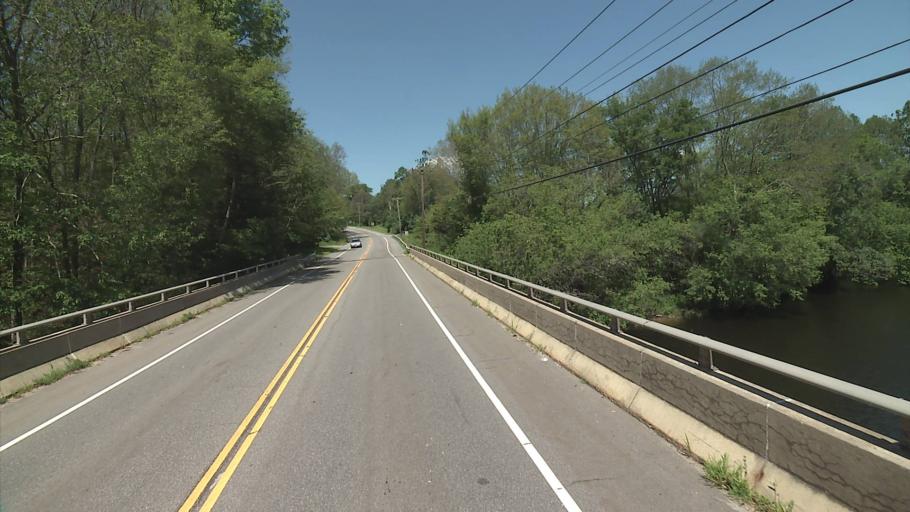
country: US
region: Connecticut
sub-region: Windham County
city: Plainfield Village
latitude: 41.6979
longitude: -71.9627
